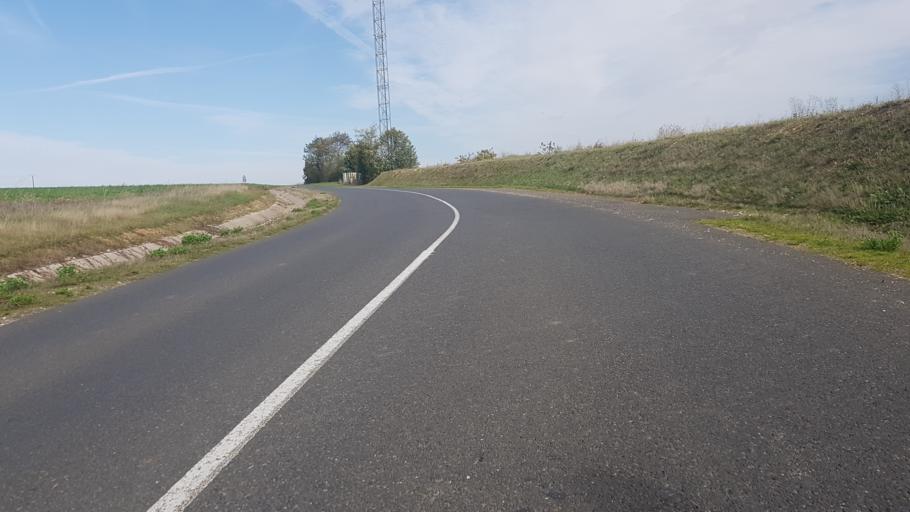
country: FR
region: Poitou-Charentes
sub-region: Departement de la Vienne
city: Chasseneuil-du-Poitou
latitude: 46.6451
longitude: 0.3496
